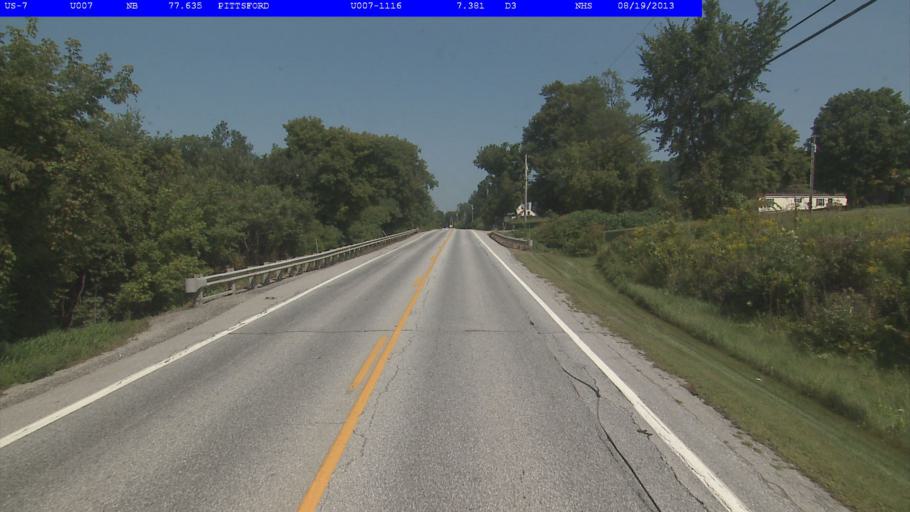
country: US
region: Vermont
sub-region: Rutland County
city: Brandon
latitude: 43.7513
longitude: -73.0478
